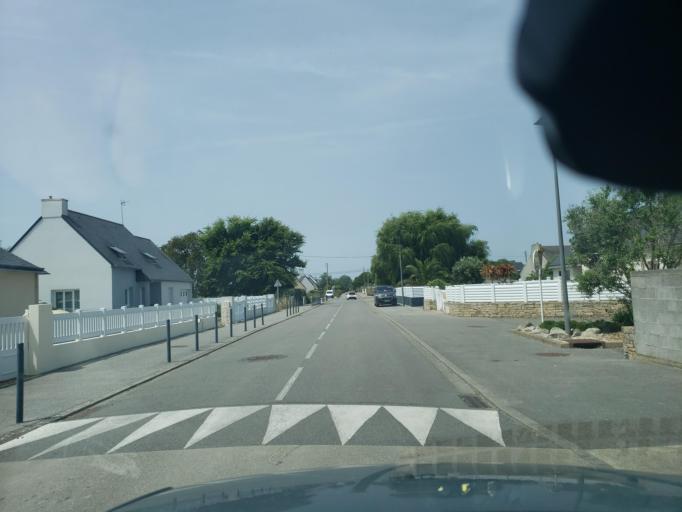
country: FR
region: Brittany
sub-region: Departement du Finistere
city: Guilvinec
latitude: 47.8011
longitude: -4.2881
